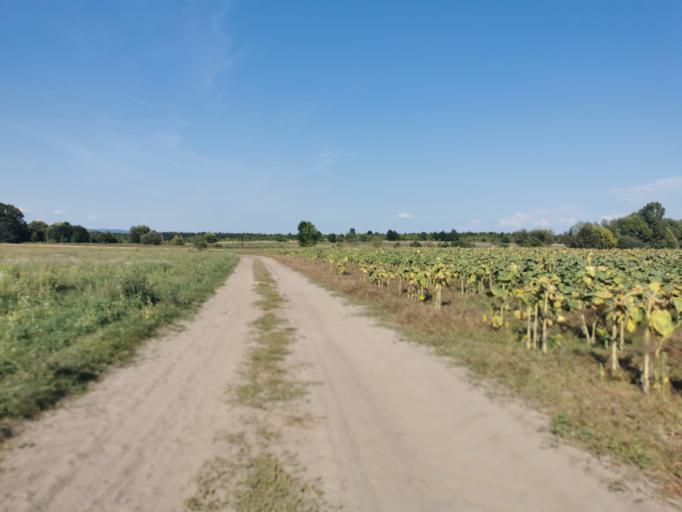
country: SK
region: Trnavsky
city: Gbely
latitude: 48.6198
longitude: 17.2209
